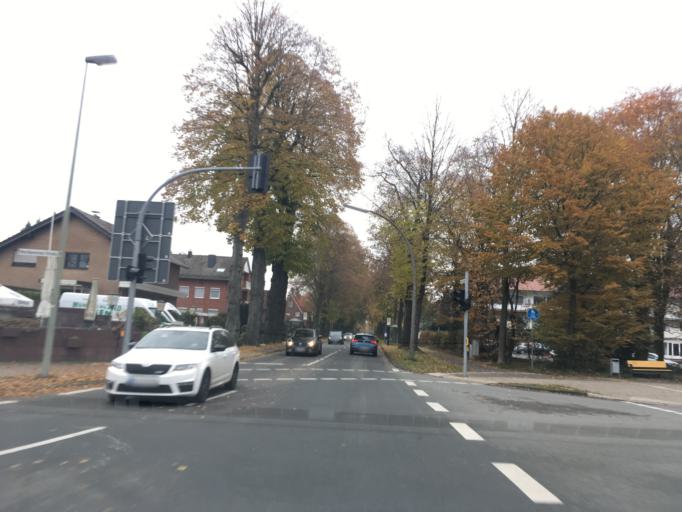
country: DE
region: North Rhine-Westphalia
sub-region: Regierungsbezirk Munster
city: Telgte
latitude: 51.9856
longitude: 7.7923
